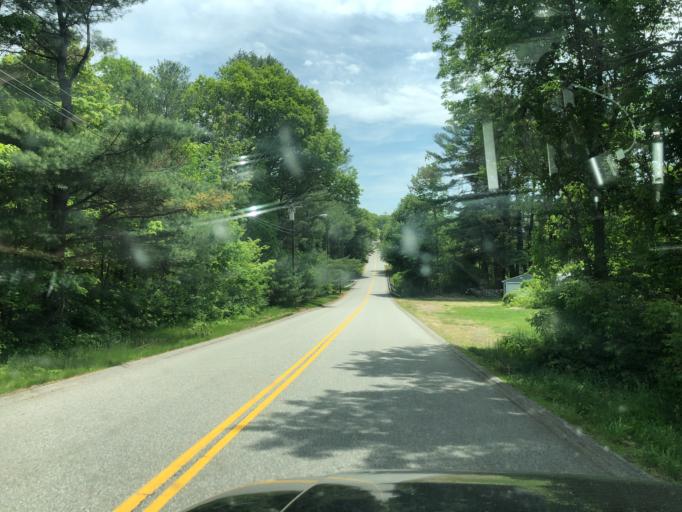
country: US
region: Connecticut
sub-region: Windham County
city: North Grosvenor Dale
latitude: 41.9748
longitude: -71.8859
